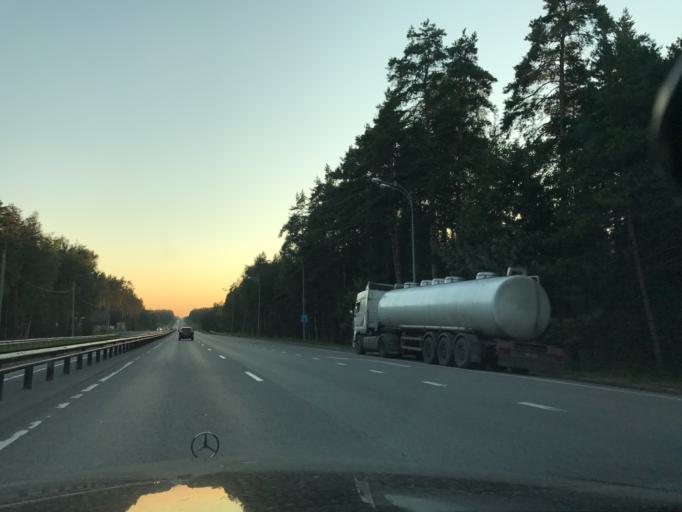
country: RU
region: Vladimir
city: Petushki
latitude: 55.9323
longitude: 39.3835
